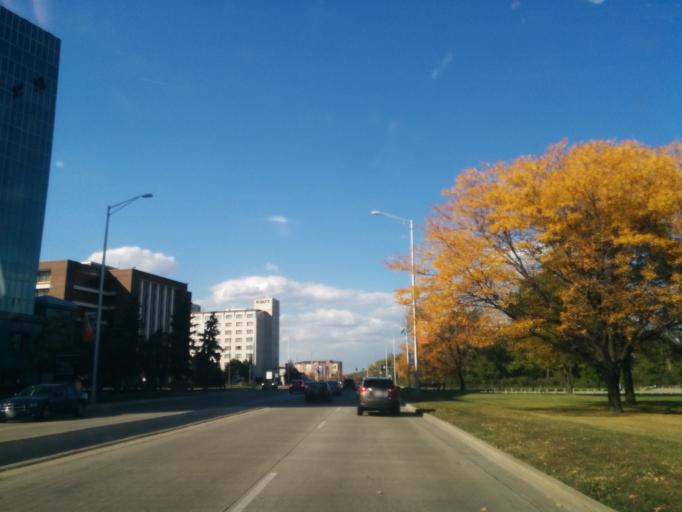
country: US
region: Illinois
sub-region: Cook County
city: Rosemont
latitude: 41.9935
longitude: -87.8607
